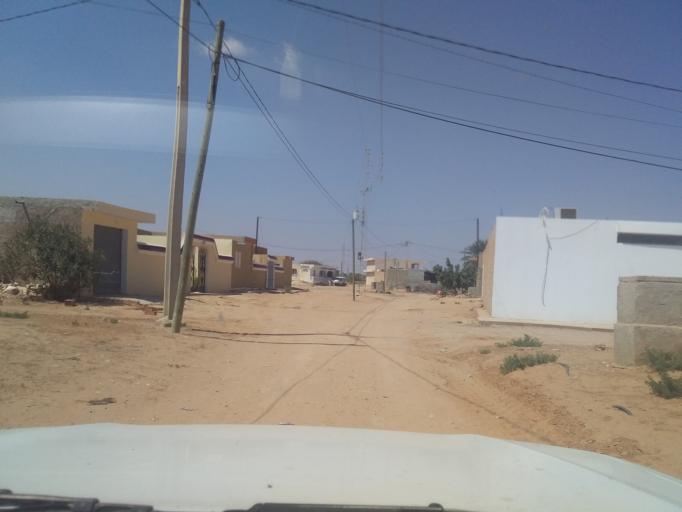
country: TN
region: Qabis
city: Matmata
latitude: 33.5940
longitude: 10.2852
